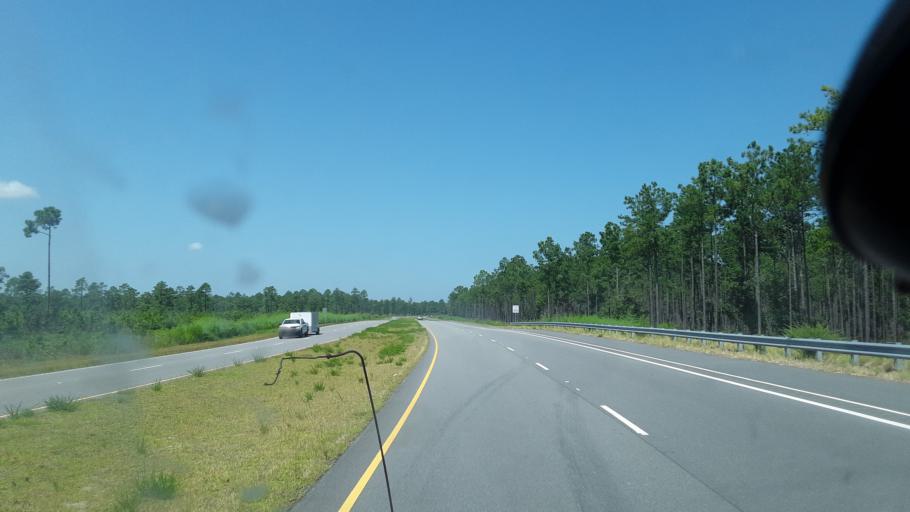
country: US
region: South Carolina
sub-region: Horry County
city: Forestbrook
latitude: 33.8034
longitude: -78.8868
